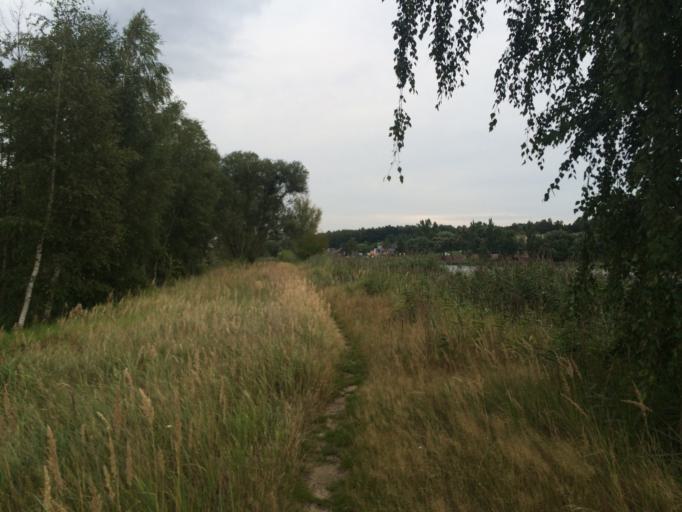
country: PL
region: Swietokrzyskie
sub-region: Powiat starachowicki
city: Starachowice
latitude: 51.0507
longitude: 21.0555
